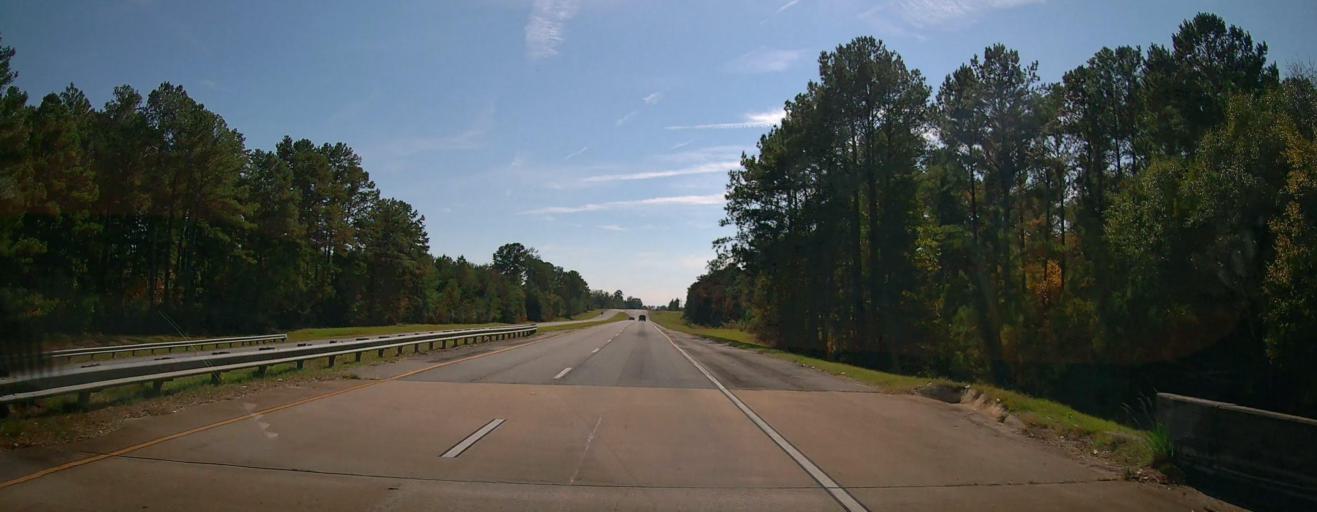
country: US
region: Georgia
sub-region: Dougherty County
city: Albany
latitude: 31.6680
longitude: -83.9967
